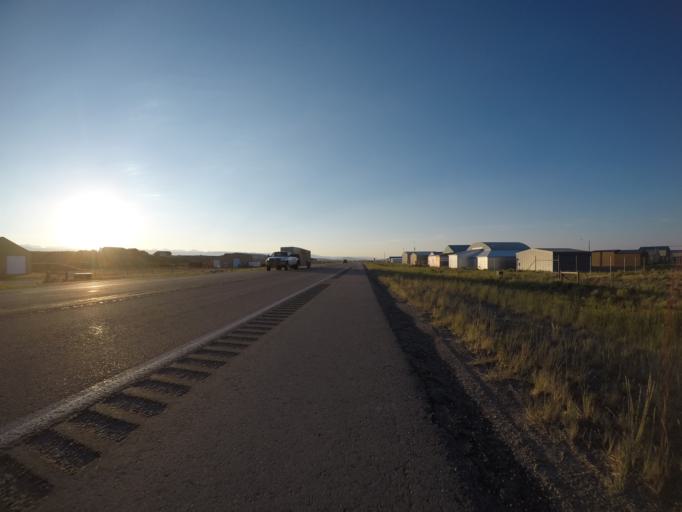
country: US
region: Wyoming
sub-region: Sublette County
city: Pinedale
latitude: 42.8002
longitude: -109.8072
